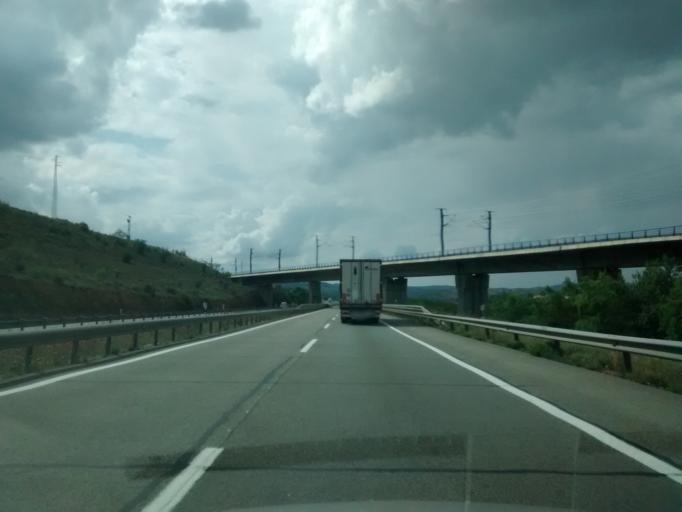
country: ES
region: Aragon
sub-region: Provincia de Zaragoza
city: Ateca
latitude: 41.3145
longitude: -1.7712
